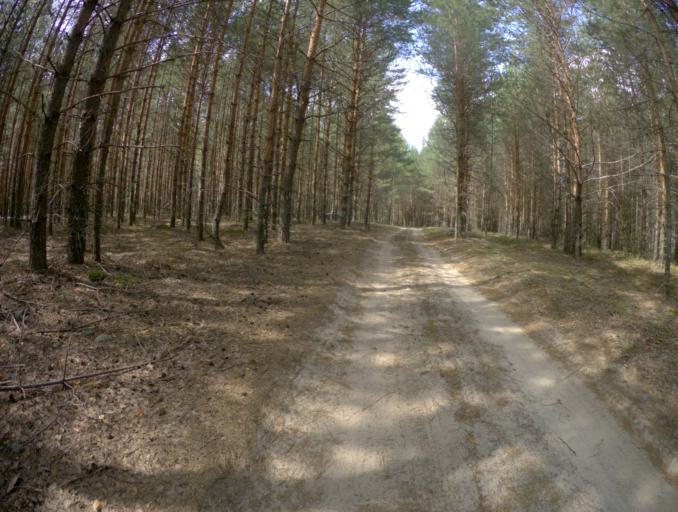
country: RU
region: Vladimir
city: Raduzhnyy
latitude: 55.9614
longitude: 40.1981
